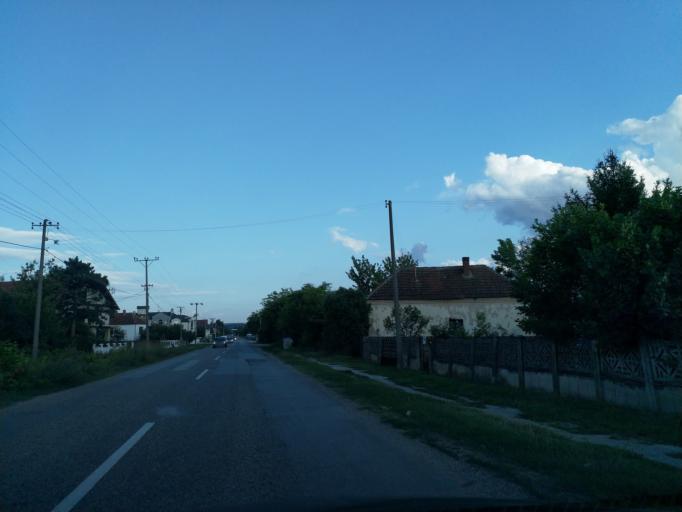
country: RS
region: Central Serbia
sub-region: Rasinski Okrug
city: Cicevac
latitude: 43.7549
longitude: 21.4363
